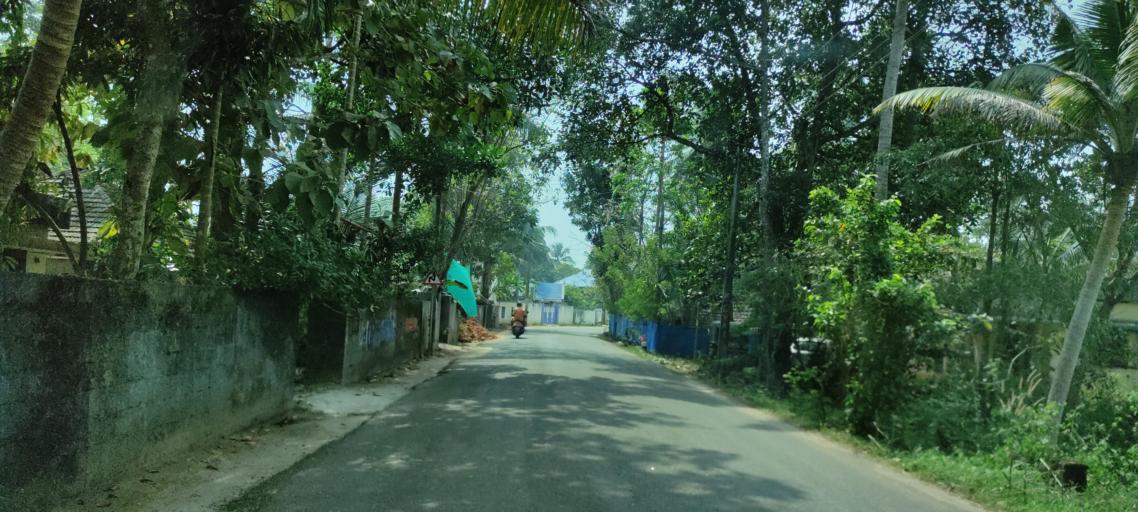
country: IN
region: Kerala
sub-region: Alappuzha
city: Shertallai
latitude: 9.6488
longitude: 76.3563
